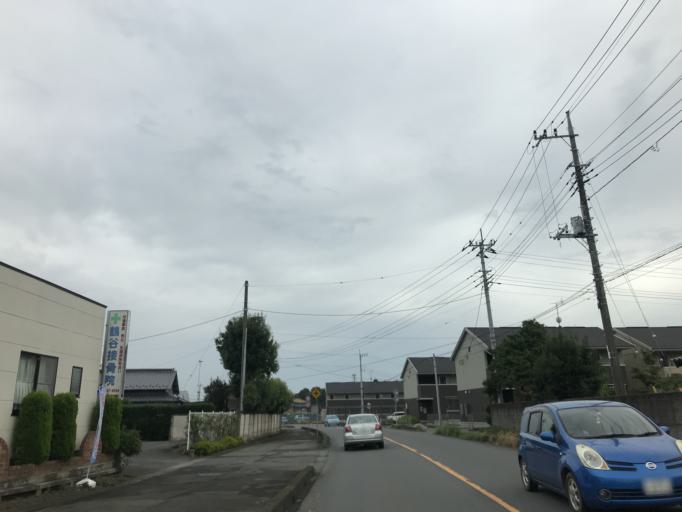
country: JP
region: Ibaraki
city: Sakai
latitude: 36.1265
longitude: 139.7930
